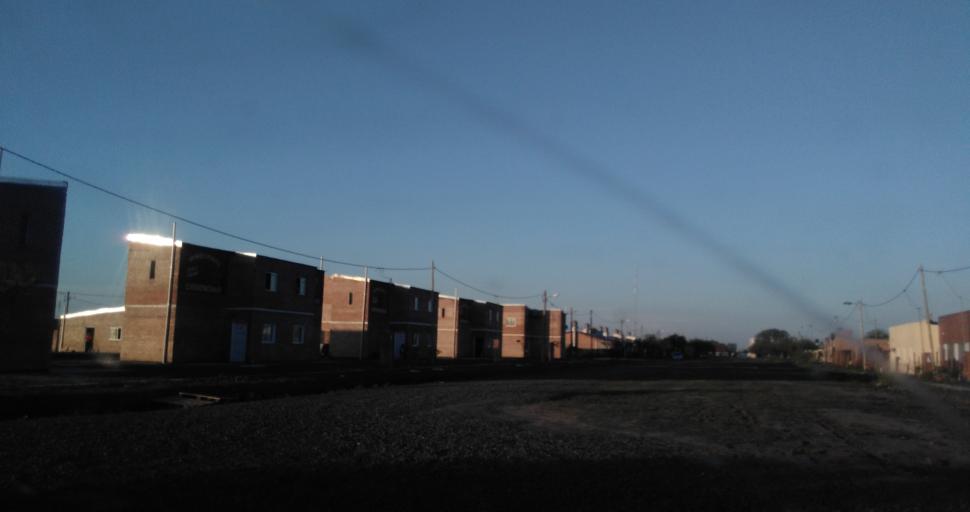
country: AR
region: Chaco
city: Resistencia
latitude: -27.4831
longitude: -59.0133
